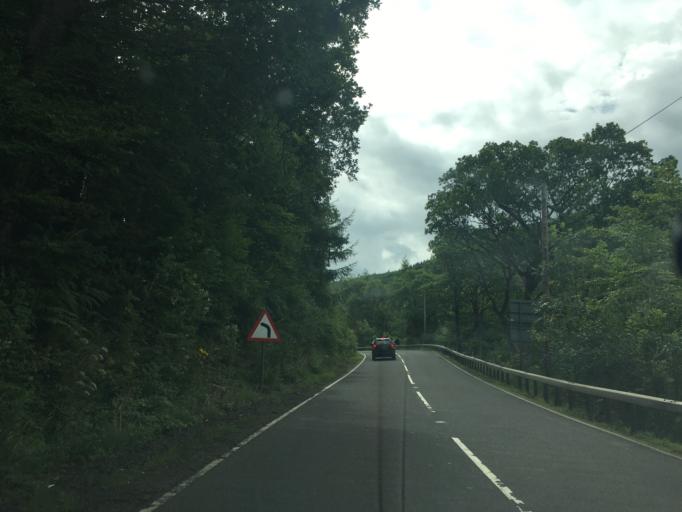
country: GB
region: Scotland
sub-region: Stirling
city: Callander
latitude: 56.2532
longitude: -4.2808
